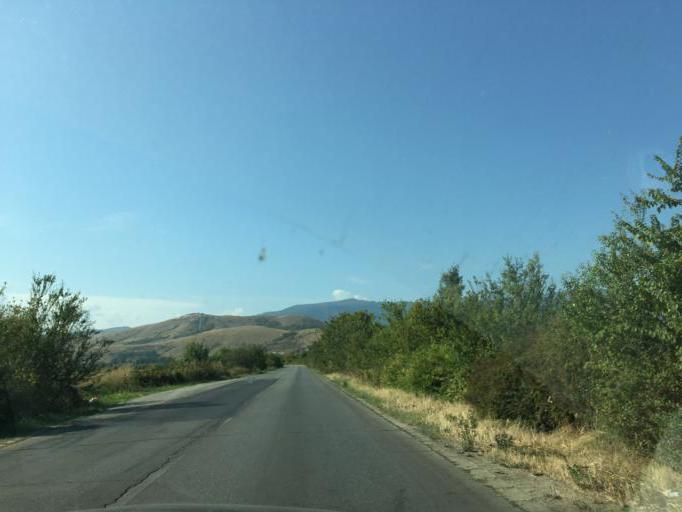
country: BG
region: Pazardzhik
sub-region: Obshtina Pazardzhik
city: Pazardzhik
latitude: 42.1357
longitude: 24.2963
